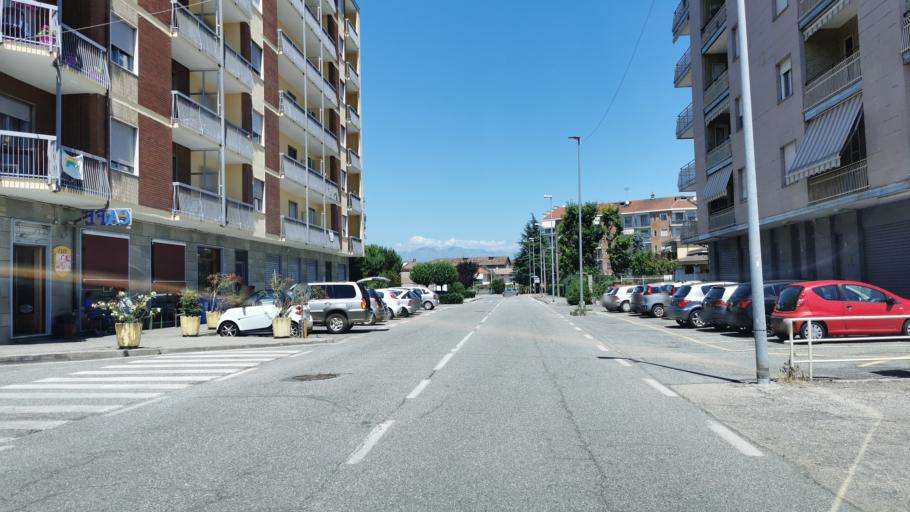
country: IT
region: Piedmont
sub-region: Provincia di Torino
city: Brandizzo
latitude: 45.1790
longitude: 7.8343
